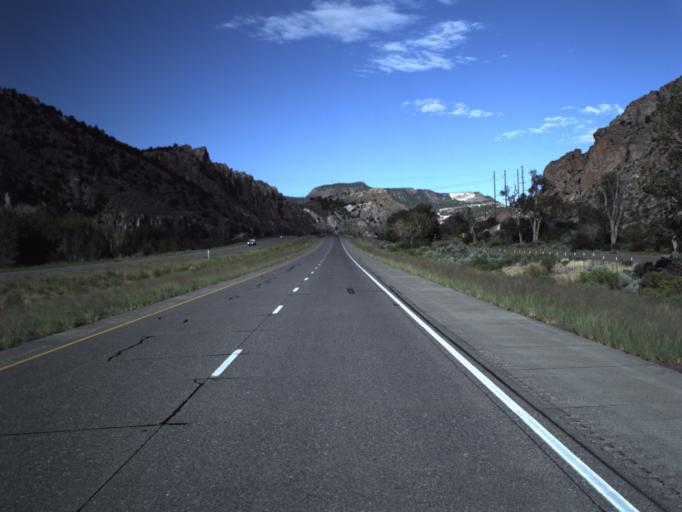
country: US
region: Utah
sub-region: Sevier County
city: Monroe
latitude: 38.5794
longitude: -112.3089
